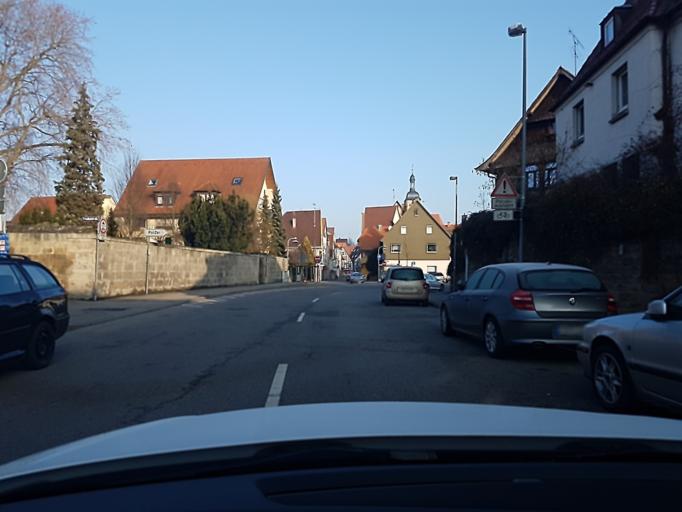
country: DE
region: Baden-Wuerttemberg
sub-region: Regierungsbezirk Stuttgart
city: Lauffen am Neckar
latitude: 49.0738
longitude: 9.1551
